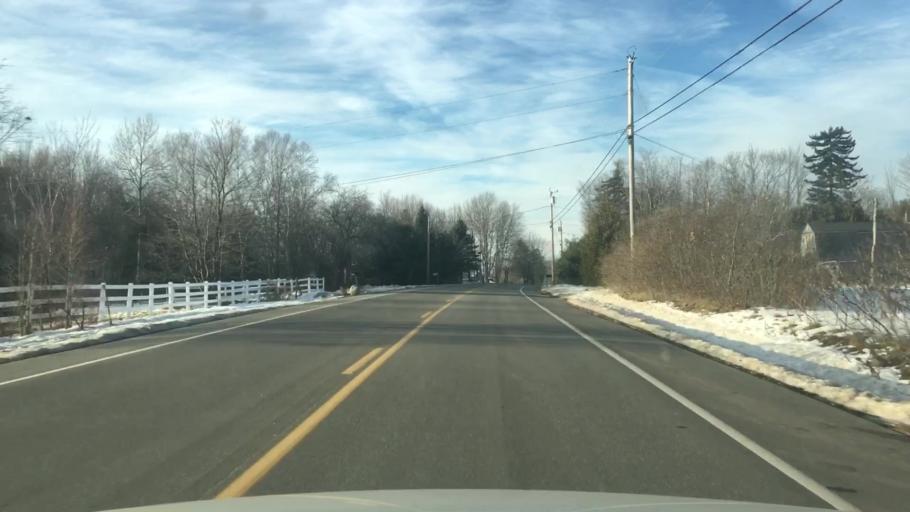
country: US
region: Maine
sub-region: Sagadahoc County
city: Richmond
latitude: 44.0926
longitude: -69.7120
